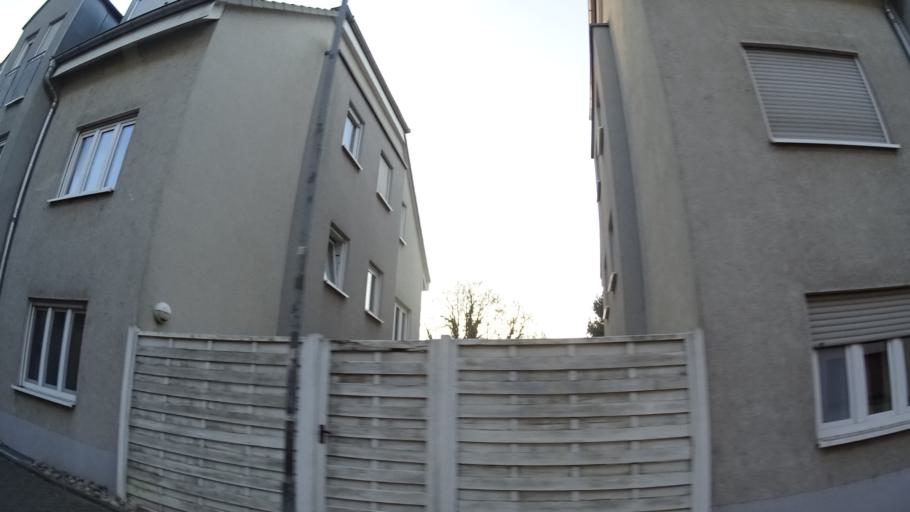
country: DE
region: Baden-Wuerttemberg
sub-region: Karlsruhe Region
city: Eppelheim
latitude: 49.4268
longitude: 8.6464
